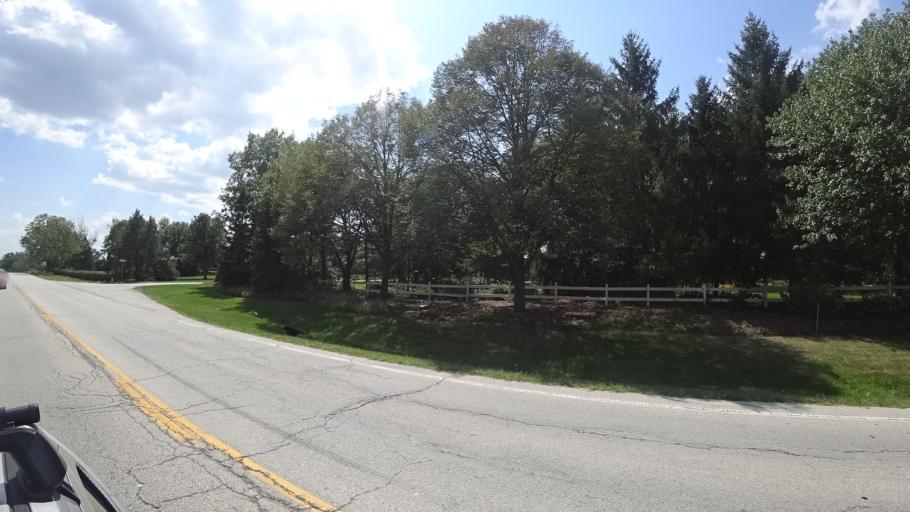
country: US
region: Illinois
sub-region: Cook County
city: Orland Park
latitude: 41.6270
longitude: -87.8195
